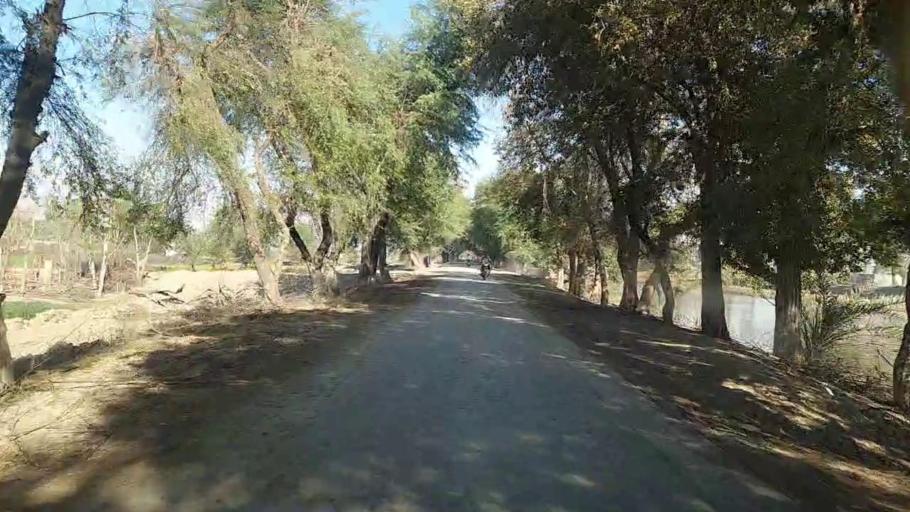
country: PK
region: Sindh
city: Khairpur
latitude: 28.0020
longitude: 69.6519
